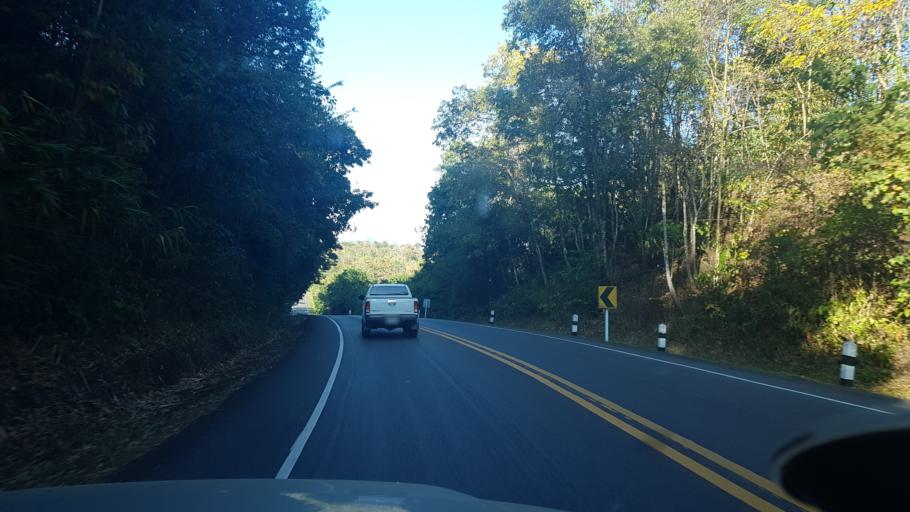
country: TH
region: Phetchabun
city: Nam Nao
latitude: 16.7613
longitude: 101.4808
